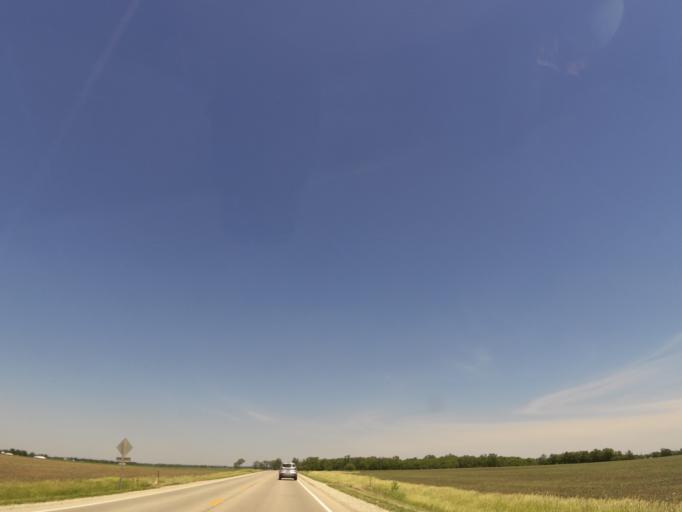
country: US
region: Illinois
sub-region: Iroquois County
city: Milford
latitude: 40.5614
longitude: -87.6935
